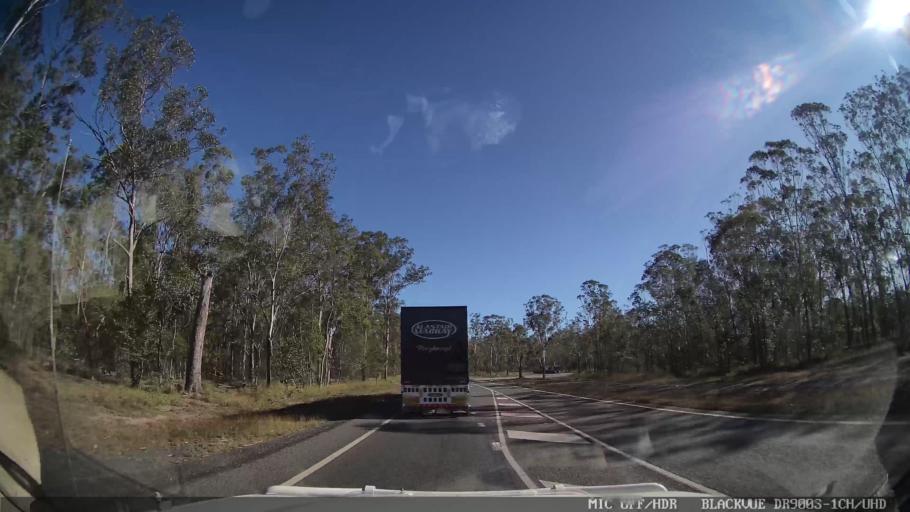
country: AU
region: Queensland
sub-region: Bundaberg
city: Childers
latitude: -25.2111
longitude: 152.0842
